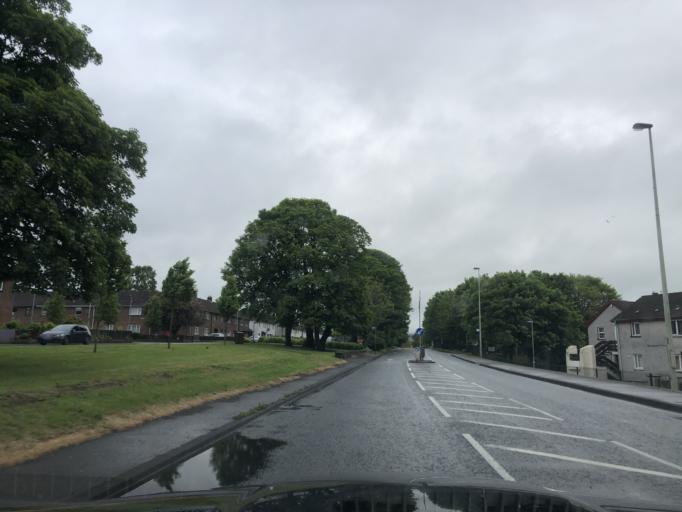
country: GB
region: Northern Ireland
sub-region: Antrim Borough
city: Antrim
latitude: 54.7065
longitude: -6.2224
